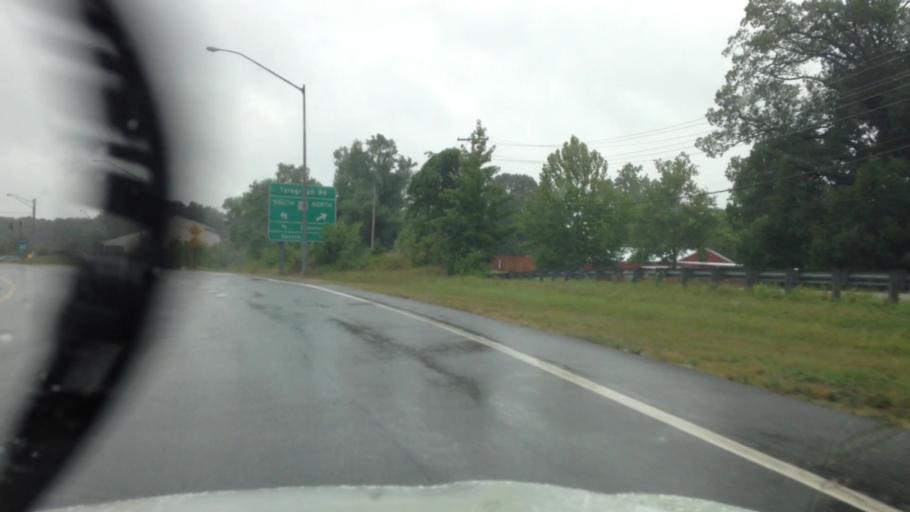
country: US
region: Maryland
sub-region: Anne Arundel County
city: Odenton
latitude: 39.1007
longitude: -76.6921
